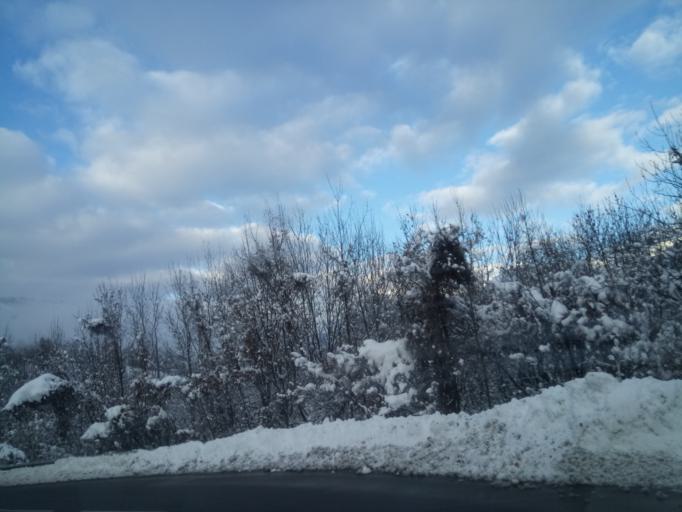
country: FR
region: Rhone-Alpes
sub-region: Departement de la Savoie
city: Saint-Jean-de-Maurienne
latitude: 45.2428
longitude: 6.3109
